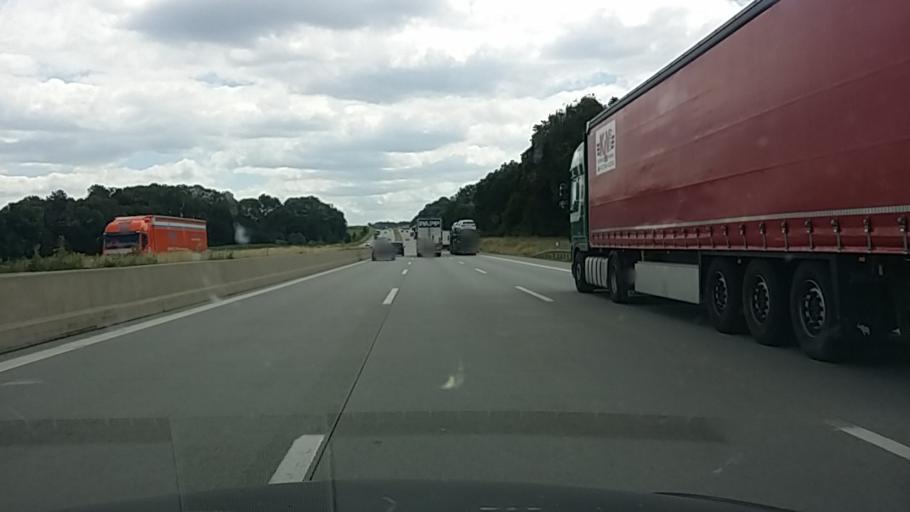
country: DE
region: Bavaria
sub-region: Swabia
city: Dasing
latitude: 48.3830
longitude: 11.0824
